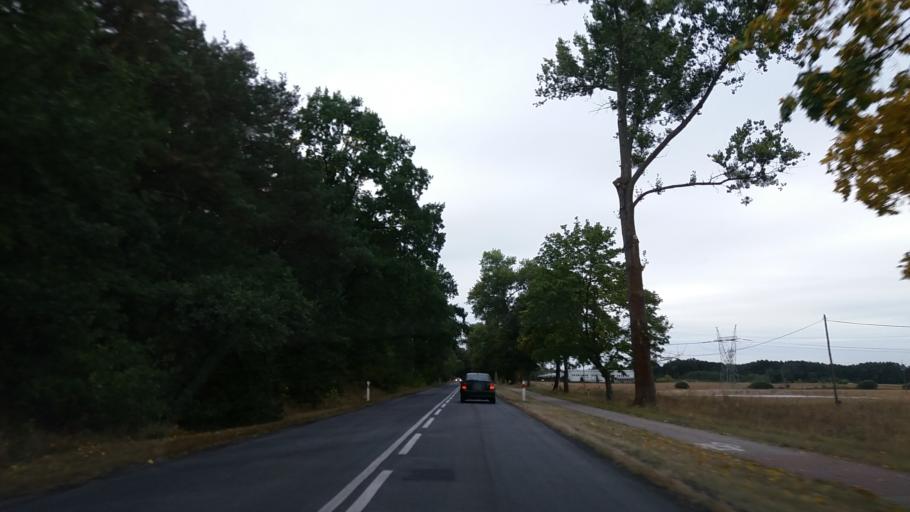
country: PL
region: Lubusz
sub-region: Powiat gorzowski
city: Klodawa
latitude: 52.7992
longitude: 15.2184
